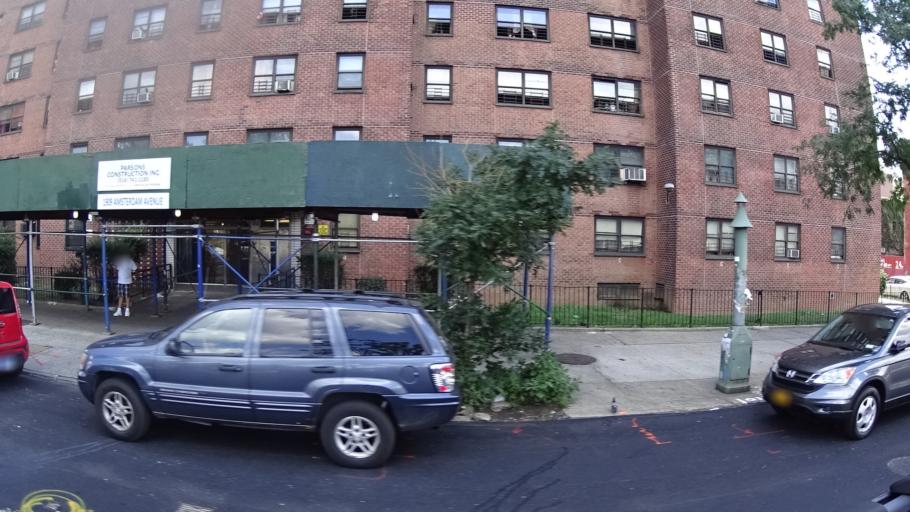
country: US
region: New Jersey
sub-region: Bergen County
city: Edgewater
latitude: 40.8312
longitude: -73.9433
